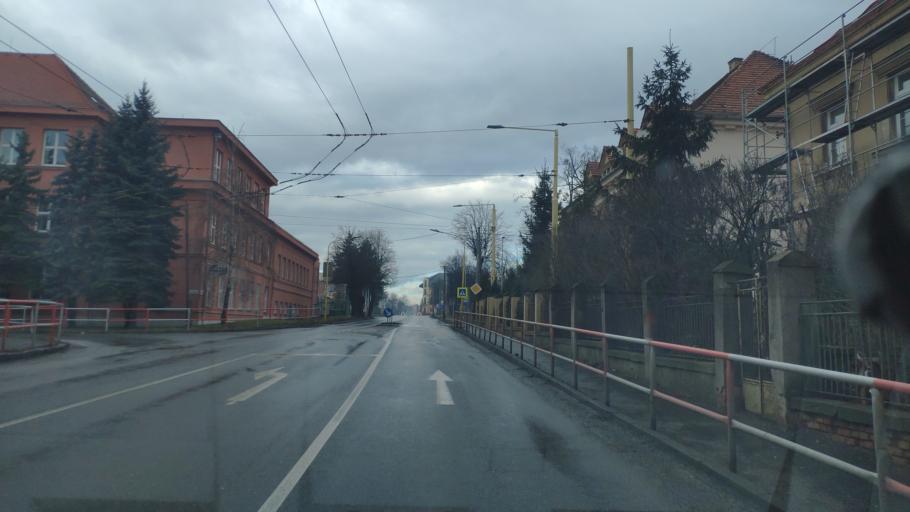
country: SK
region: Presovsky
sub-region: Okres Presov
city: Presov
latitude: 48.9915
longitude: 21.2503
